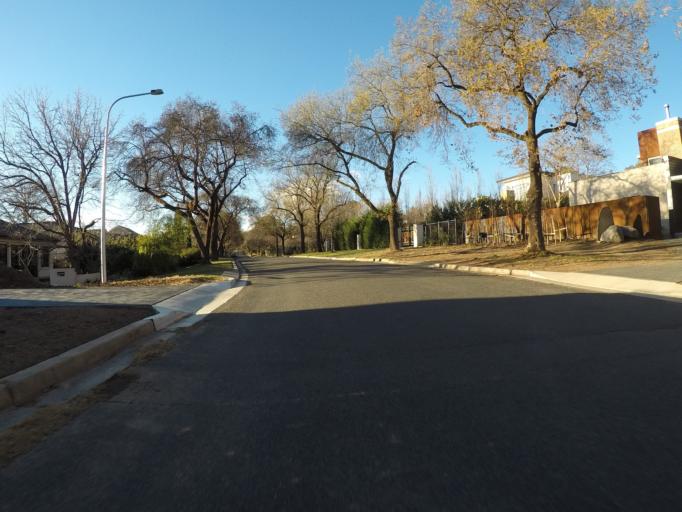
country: AU
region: Australian Capital Territory
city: Forrest
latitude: -35.3046
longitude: 149.1082
